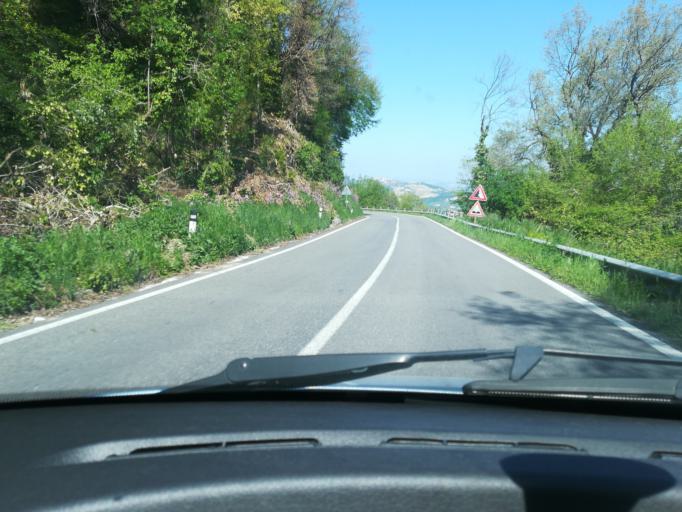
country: IT
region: The Marches
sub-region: Provincia di Macerata
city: Cingoli
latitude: 43.3803
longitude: 13.2115
